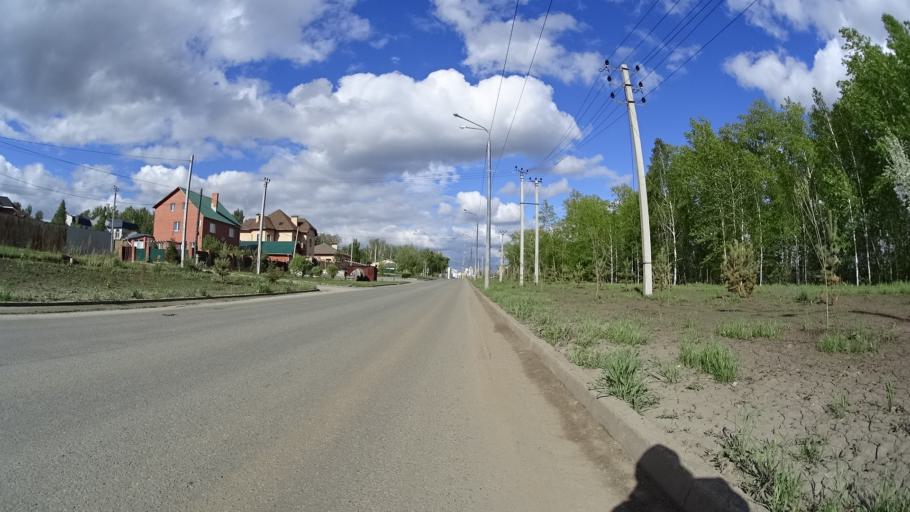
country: RU
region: Chelyabinsk
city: Sargazy
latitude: 55.1546
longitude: 61.2790
